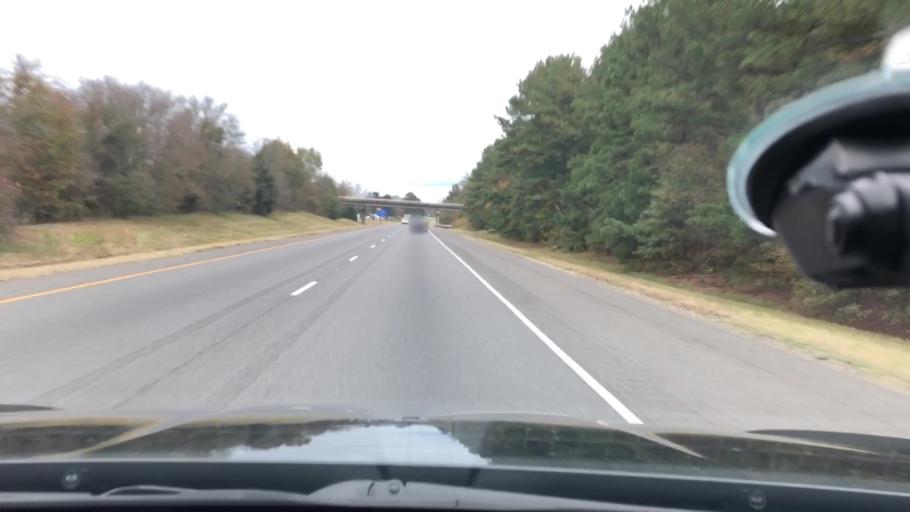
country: US
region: Arkansas
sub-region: Hot Spring County
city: Malvern
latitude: 34.3465
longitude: -92.8982
